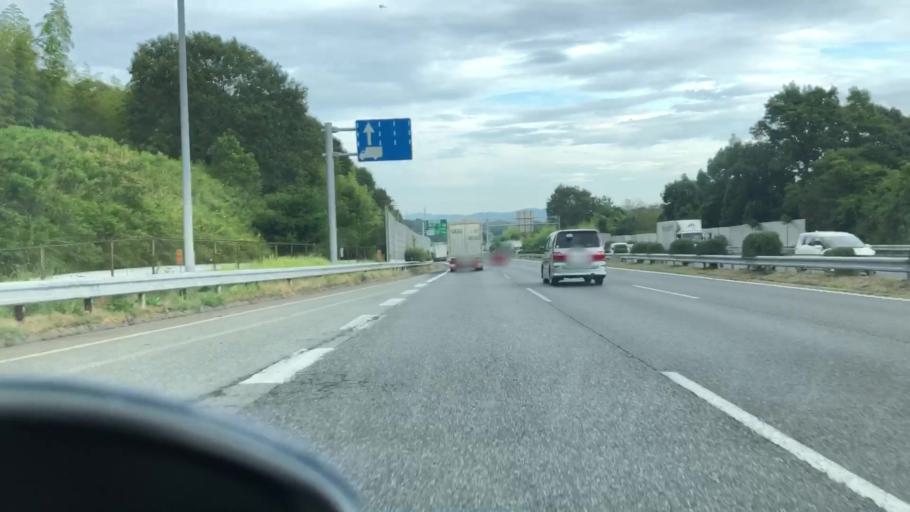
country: JP
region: Hyogo
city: Sandacho
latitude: 34.8849
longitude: 135.1730
